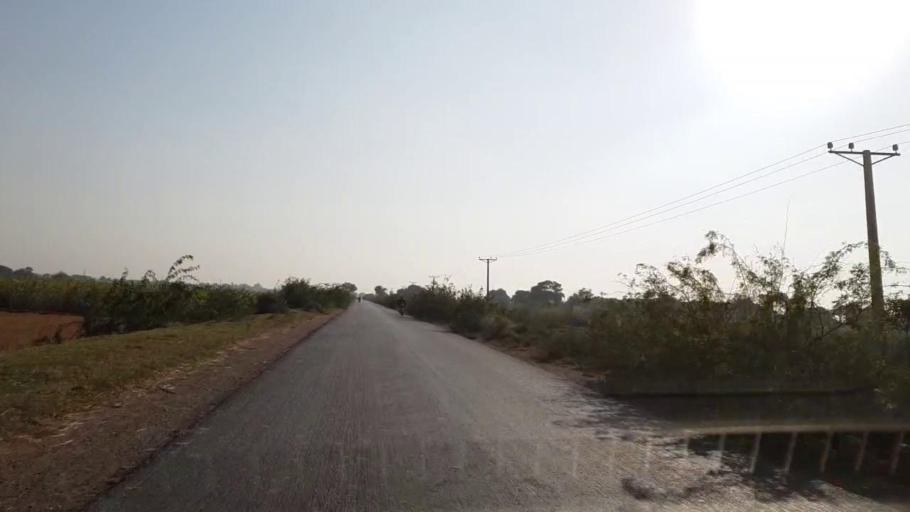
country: PK
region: Sindh
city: Bulri
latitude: 24.8881
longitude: 68.3432
